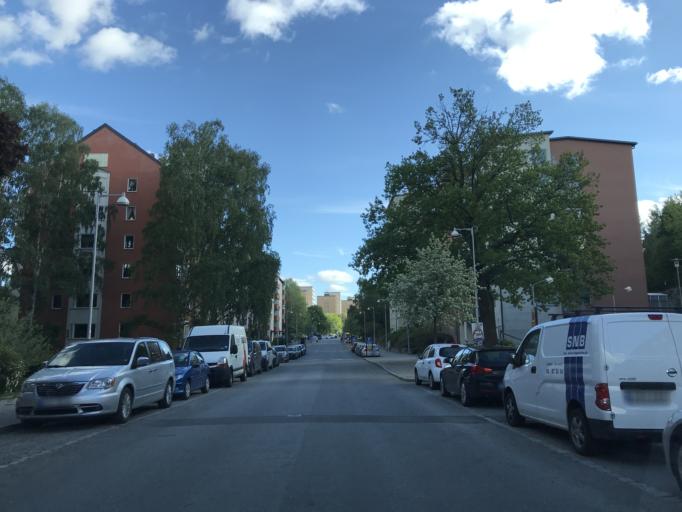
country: SE
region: Stockholm
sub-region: Solna Kommun
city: Solna
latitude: 59.3516
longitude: 17.9968
